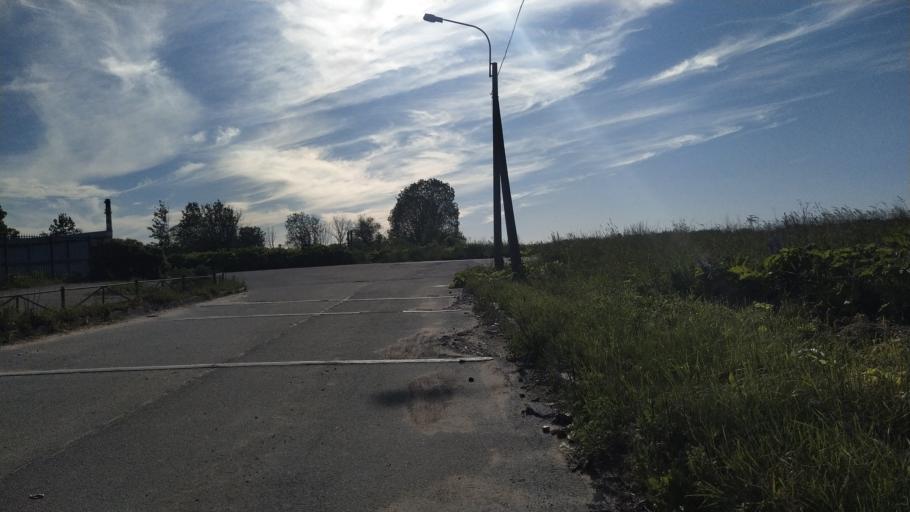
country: RU
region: St.-Petersburg
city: Pushkin
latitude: 59.7406
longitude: 30.3854
